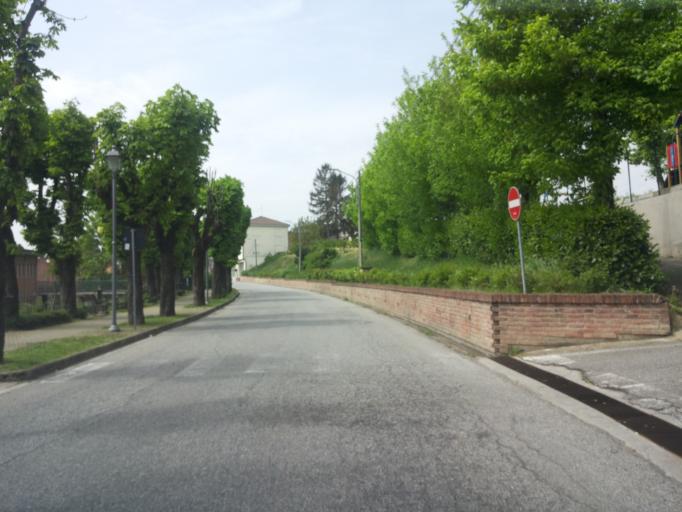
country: IT
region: Piedmont
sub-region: Provincia di Alessandria
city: Lu
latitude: 45.0038
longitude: 8.4912
